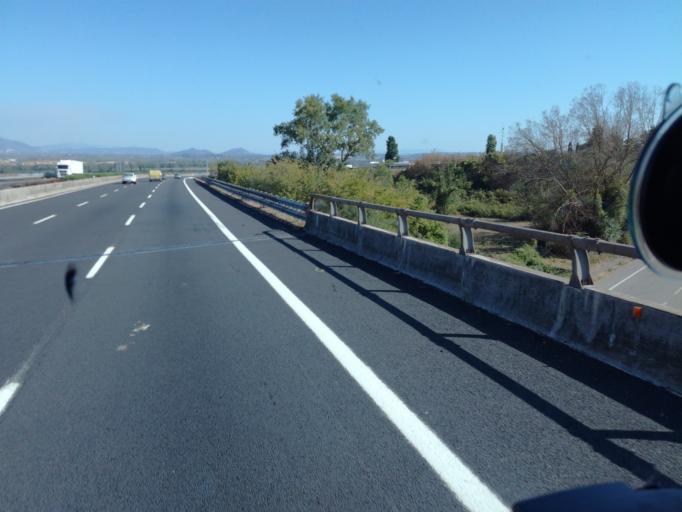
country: IT
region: Latium
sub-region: Citta metropolitana di Roma Capitale
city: Fiano Romano
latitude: 42.1613
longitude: 12.6198
